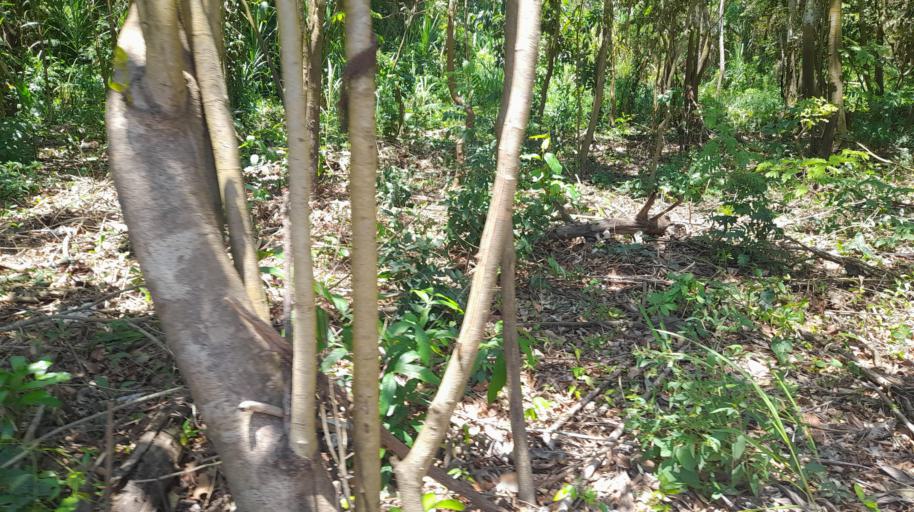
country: PE
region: Ucayali
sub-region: Provincia de Coronel Portillo
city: Puerto Callao
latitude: -8.2635
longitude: -74.6390
